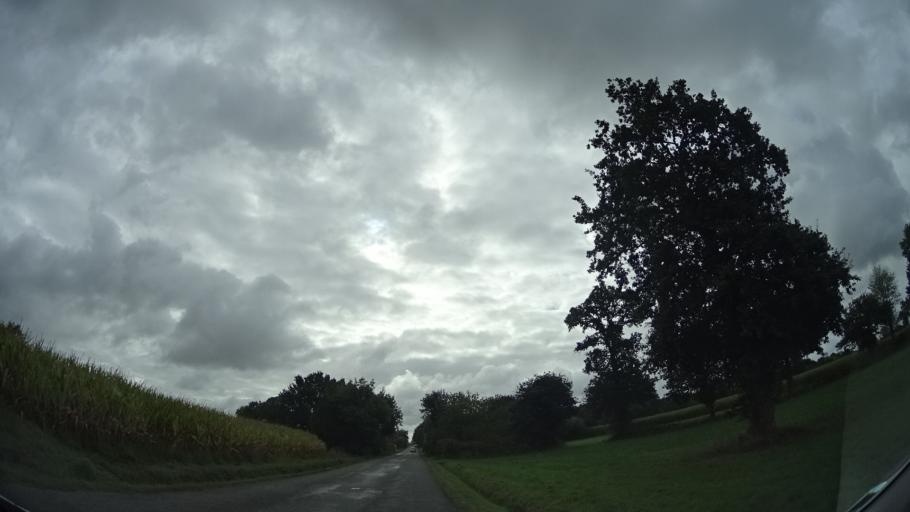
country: FR
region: Brittany
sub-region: Departement d'Ille-et-Vilaine
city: Montreuil-sur-Ille
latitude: 48.3023
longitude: -1.6566
